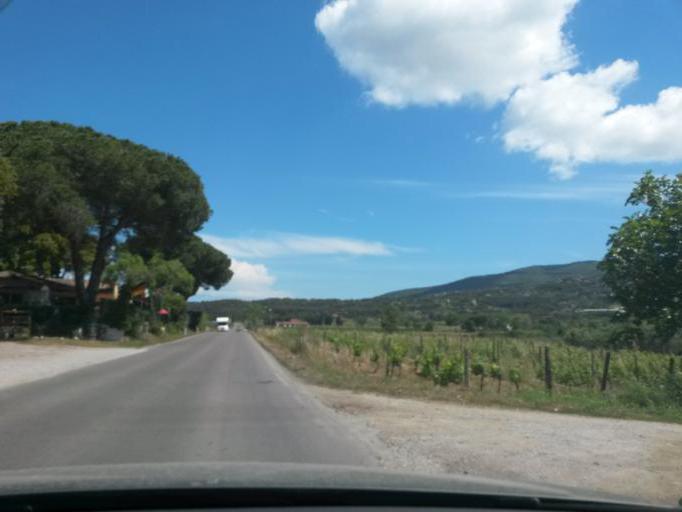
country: IT
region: Tuscany
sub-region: Provincia di Livorno
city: Capoliveri
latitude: 42.7611
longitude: 10.3657
